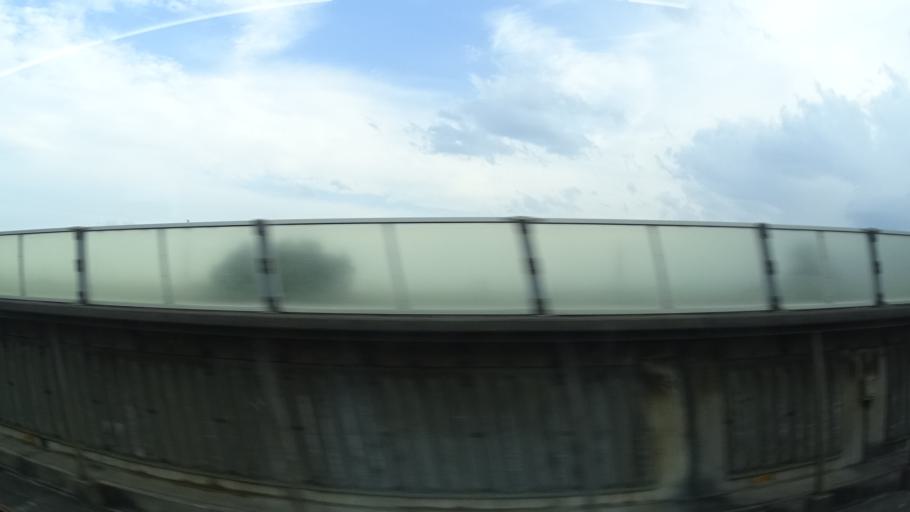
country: JP
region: Saitama
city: Fukayacho
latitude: 36.1540
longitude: 139.3236
